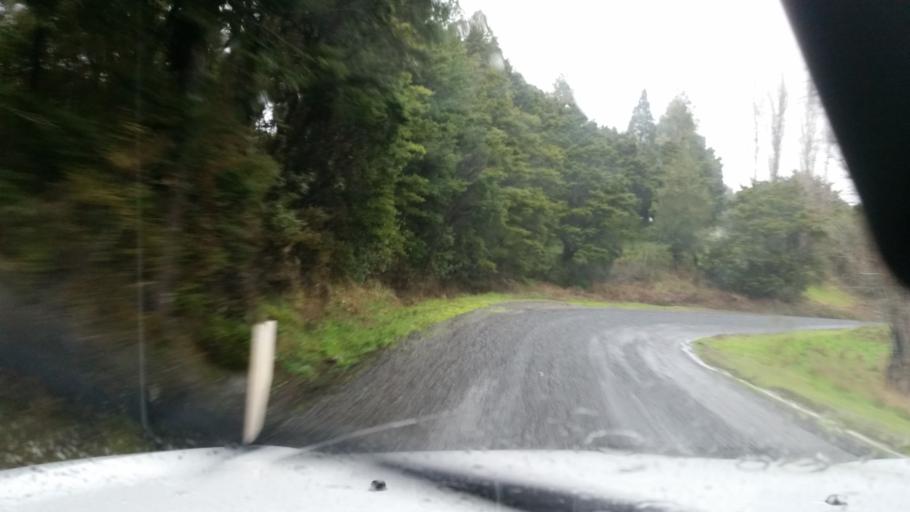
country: NZ
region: Northland
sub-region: Kaipara District
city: Dargaville
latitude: -35.7306
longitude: 173.9599
